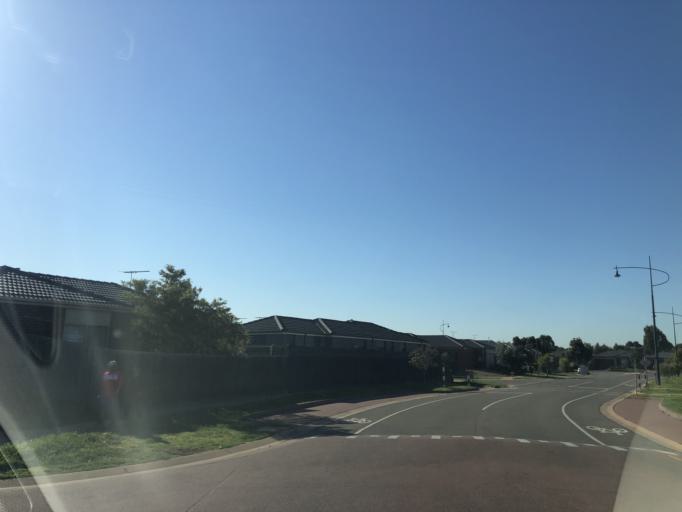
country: AU
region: Victoria
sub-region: Wyndham
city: Hoppers Crossing
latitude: -37.8943
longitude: 144.7243
